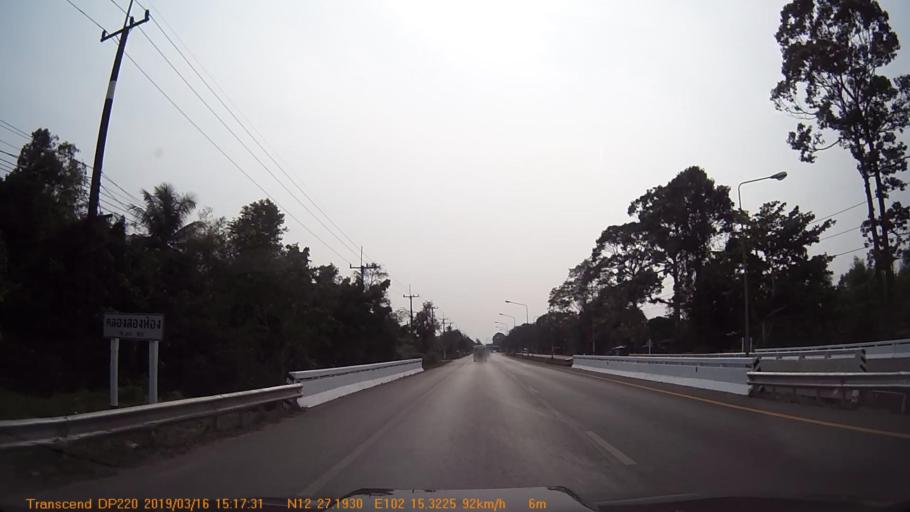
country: TH
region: Chanthaburi
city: Khlung
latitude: 12.4531
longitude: 102.2550
